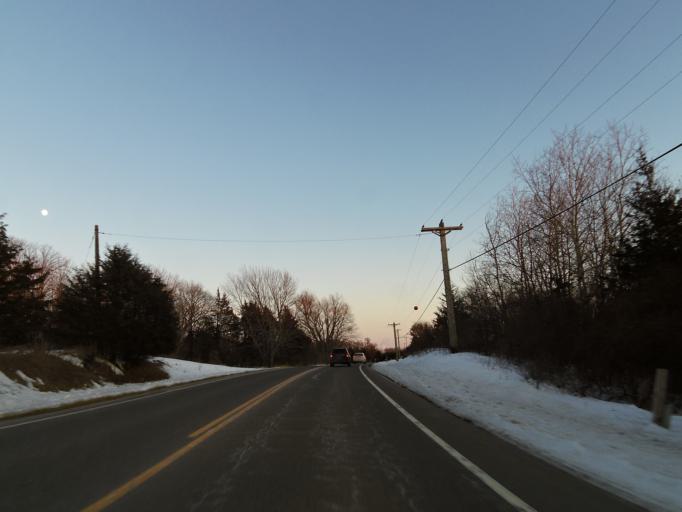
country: US
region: Minnesota
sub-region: Washington County
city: Grant
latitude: 45.0863
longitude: -92.9329
